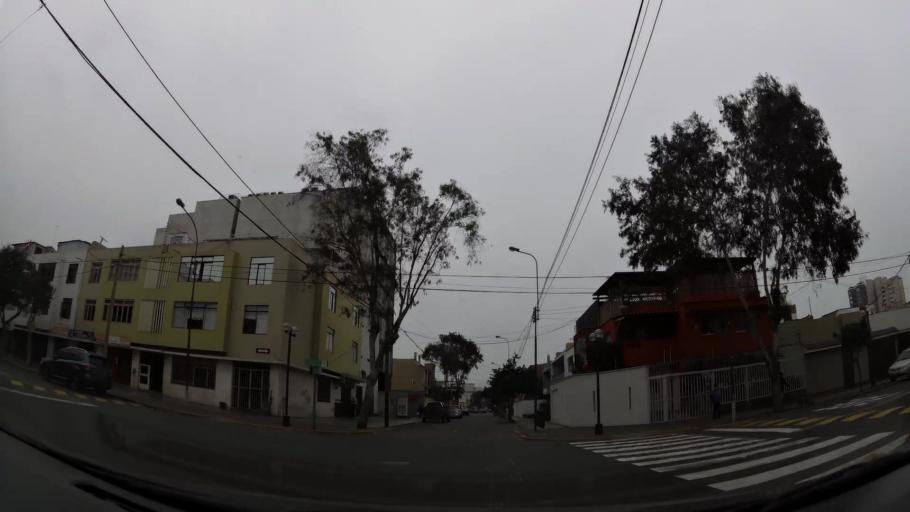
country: PE
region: Lima
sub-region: Lima
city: San Isidro
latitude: -12.1124
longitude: -77.0478
